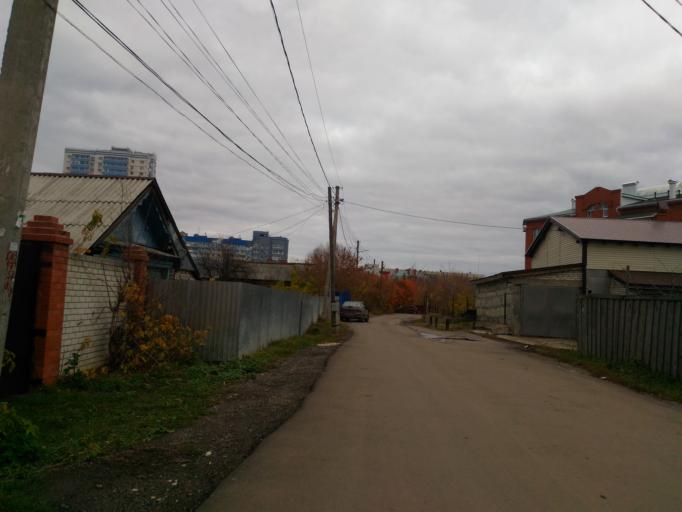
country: RU
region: Ulyanovsk
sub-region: Ulyanovskiy Rayon
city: Ulyanovsk
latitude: 54.3372
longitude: 48.3916
